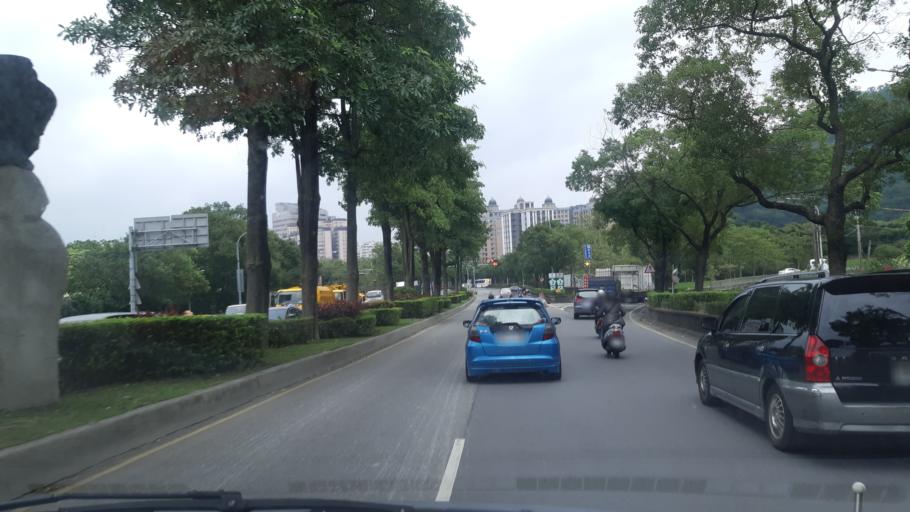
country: TW
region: Taiwan
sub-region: Taoyuan
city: Taoyuan
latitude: 24.9403
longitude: 121.3570
